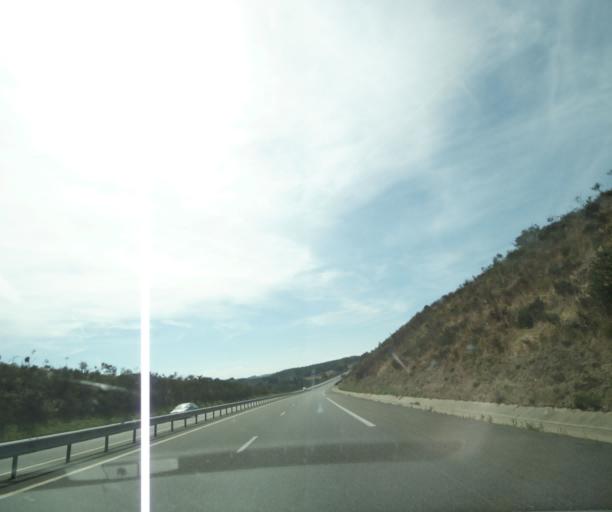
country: FR
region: Auvergne
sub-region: Departement du Puy-de-Dome
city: Charbonnieres-les-Varennes
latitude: 45.9126
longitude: 2.9562
